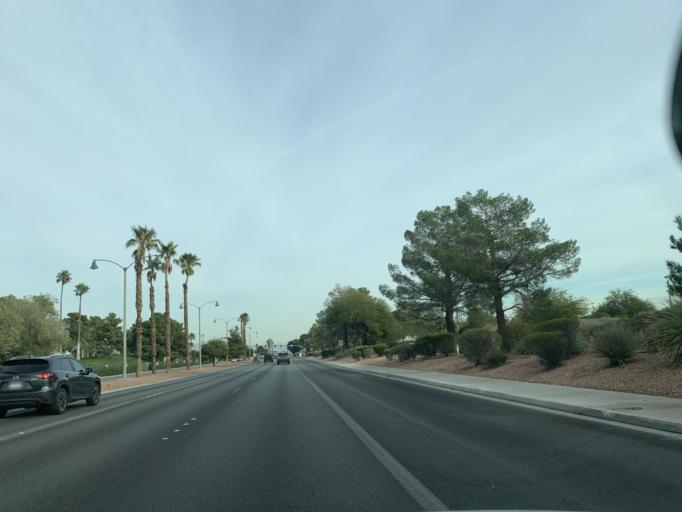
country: US
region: Nevada
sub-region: Clark County
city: Summerlin South
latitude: 36.1439
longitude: -115.2863
